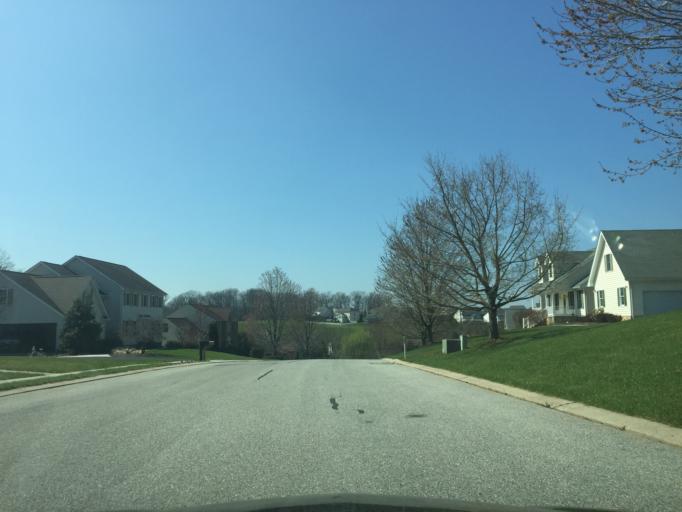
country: US
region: Pennsylvania
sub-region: York County
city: New Freedom
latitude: 39.7216
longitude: -76.6954
